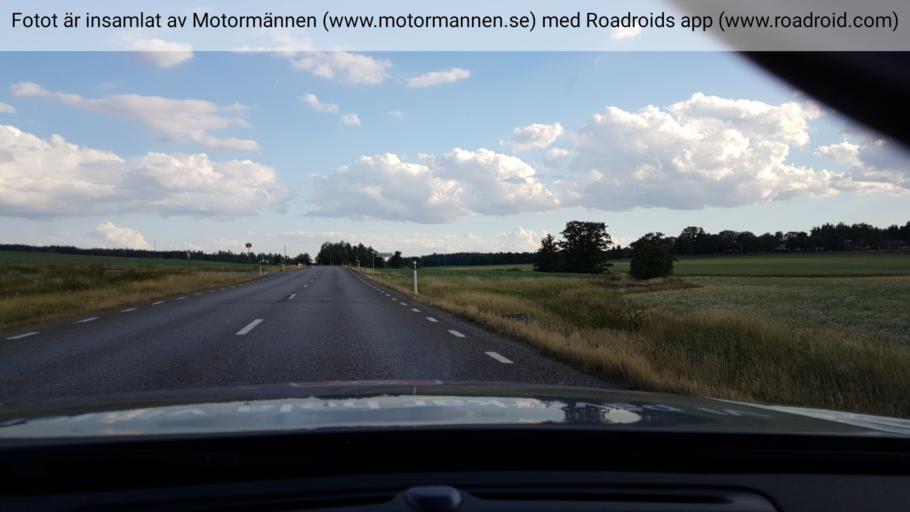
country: SE
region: Uppsala
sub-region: Heby Kommun
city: Morgongava
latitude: 59.8221
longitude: 16.9237
